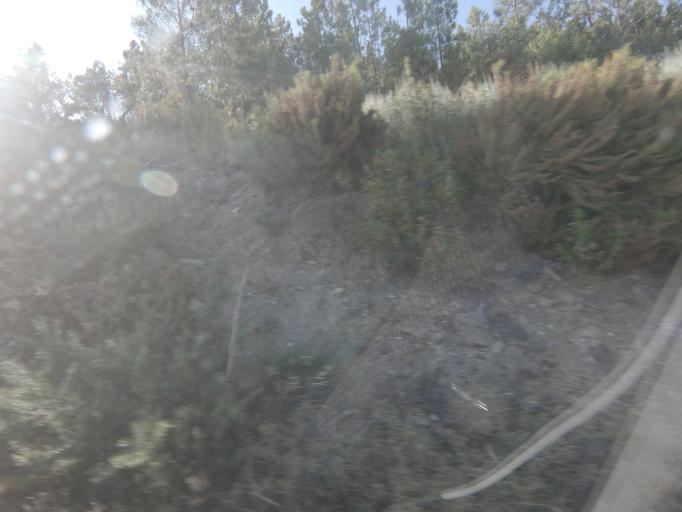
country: PT
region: Vila Real
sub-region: Sabrosa
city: Vilela
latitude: 41.1858
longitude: -7.6129
